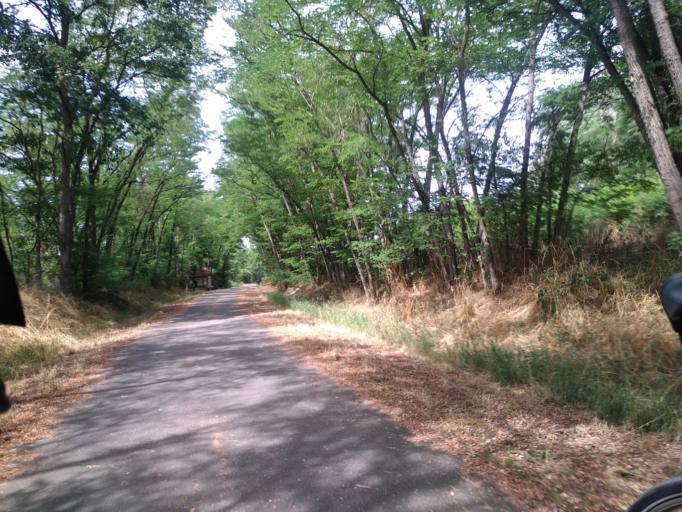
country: FR
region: Auvergne
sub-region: Departement de l'Allier
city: Diou
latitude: 46.5504
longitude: 3.7416
